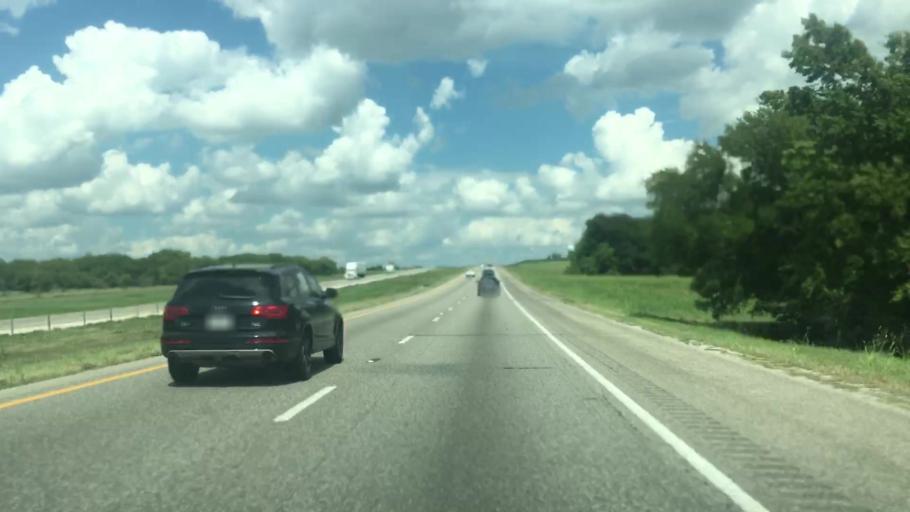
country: US
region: Texas
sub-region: Hill County
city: Hillsboro
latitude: 32.0678
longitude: -97.0722
